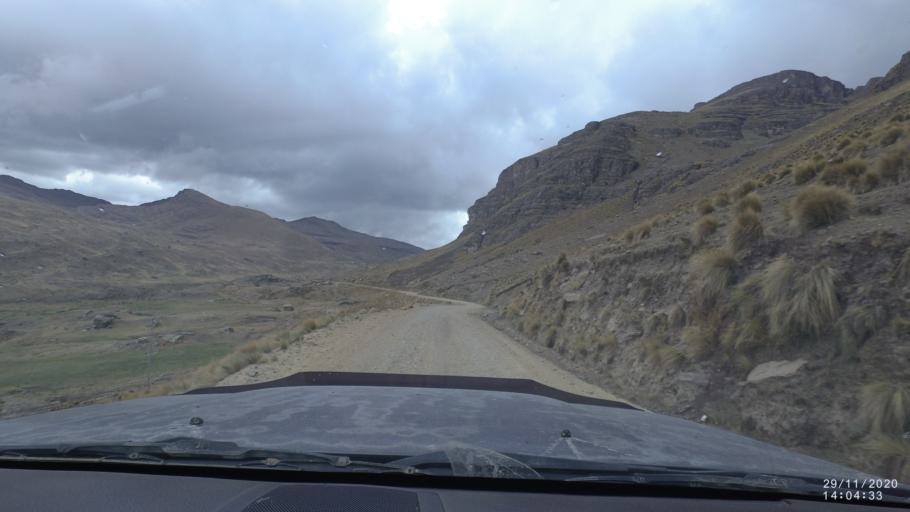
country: BO
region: Cochabamba
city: Sipe Sipe
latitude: -17.2015
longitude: -66.3770
